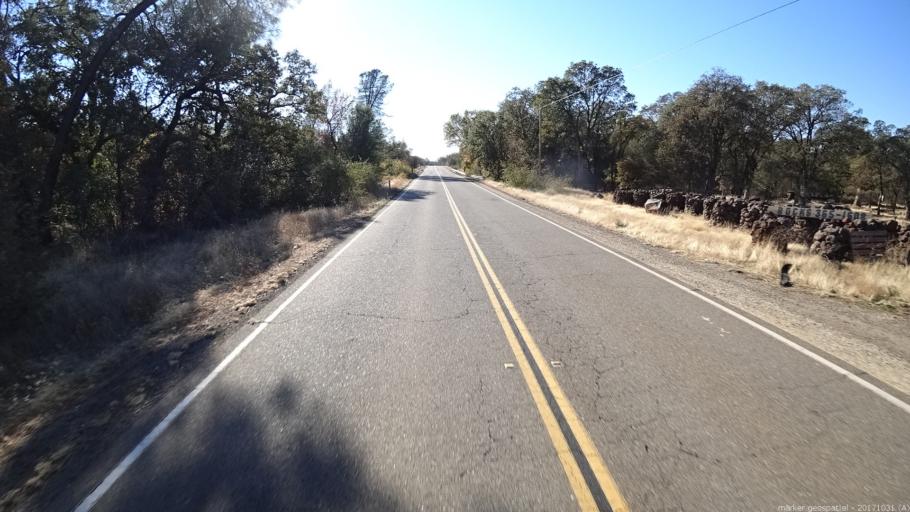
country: US
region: California
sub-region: Shasta County
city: Palo Cedro
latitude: 40.4882
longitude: -122.0722
